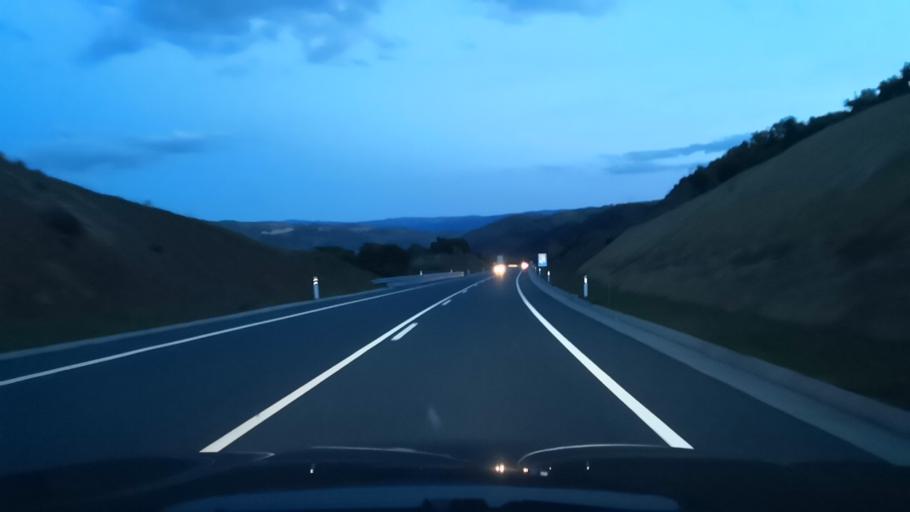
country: PT
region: Braganca
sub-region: Alfandega da Fe
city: Alfandega da Fe
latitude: 41.3218
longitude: -6.9316
